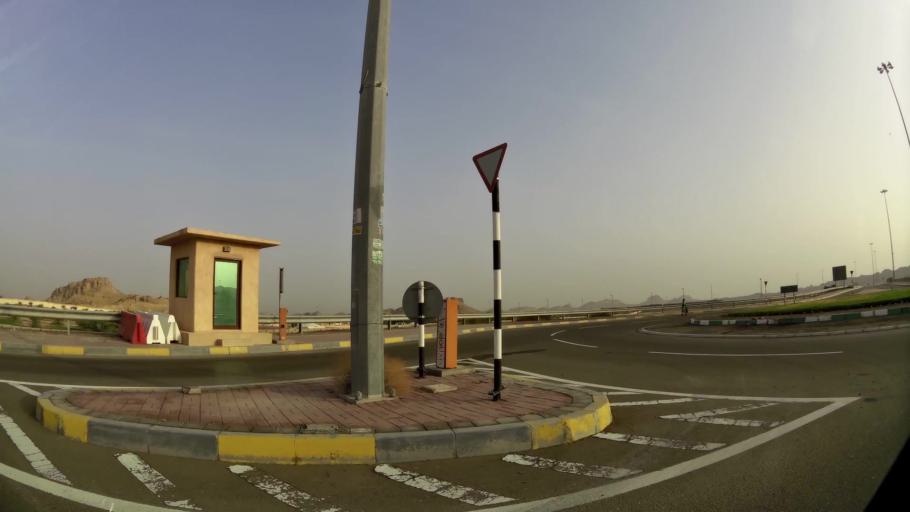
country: AE
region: Abu Dhabi
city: Al Ain
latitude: 24.1113
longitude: 55.7526
